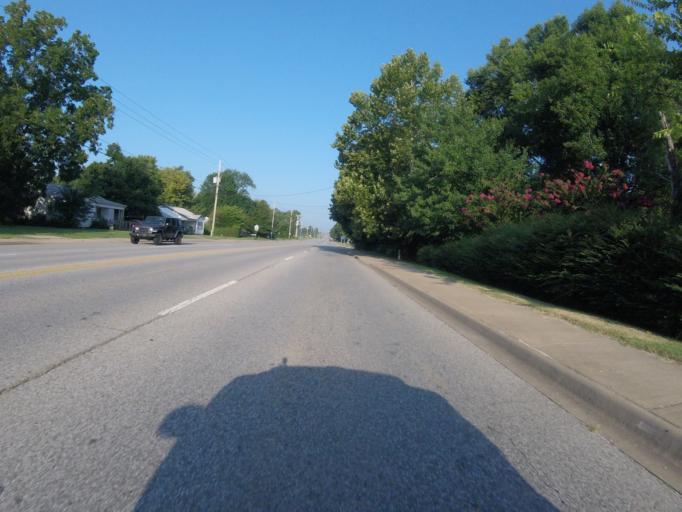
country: US
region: Arkansas
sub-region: Washington County
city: Fayetteville
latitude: 36.0781
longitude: -94.1914
